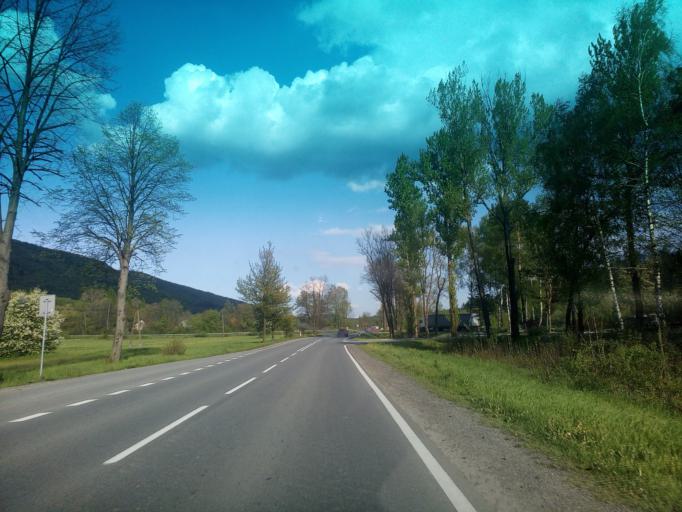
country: PL
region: Lesser Poland Voivodeship
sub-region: Powiat nowosadecki
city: Kamionka Wielka
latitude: 49.5404
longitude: 20.7987
